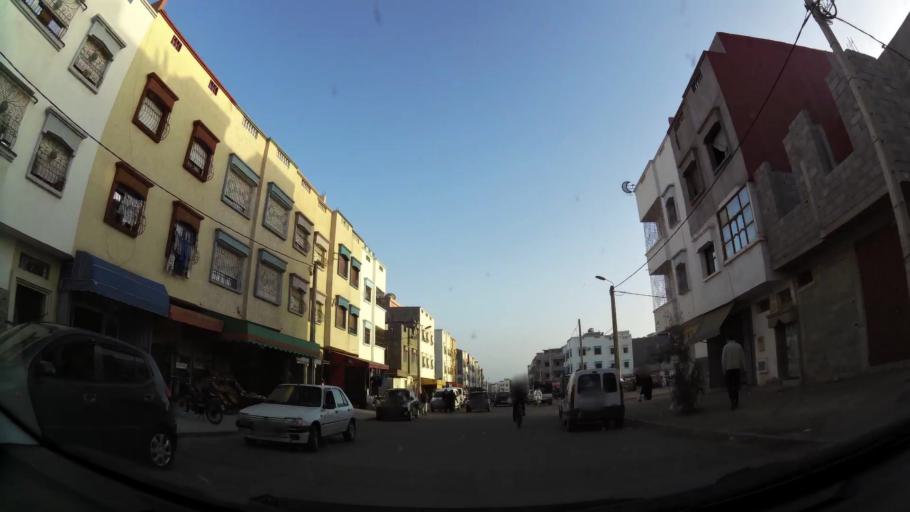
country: MA
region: Oued ed Dahab-Lagouira
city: Dakhla
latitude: 30.3976
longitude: -9.5613
